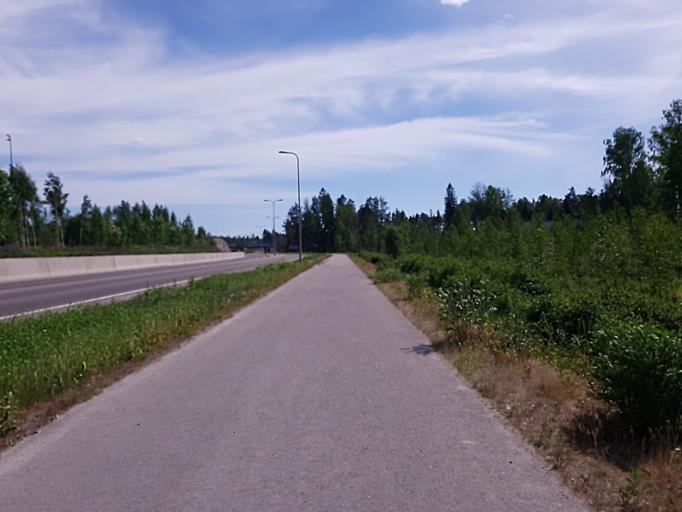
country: FI
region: Uusimaa
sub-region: Helsinki
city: Vantaa
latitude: 60.3009
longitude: 24.9160
